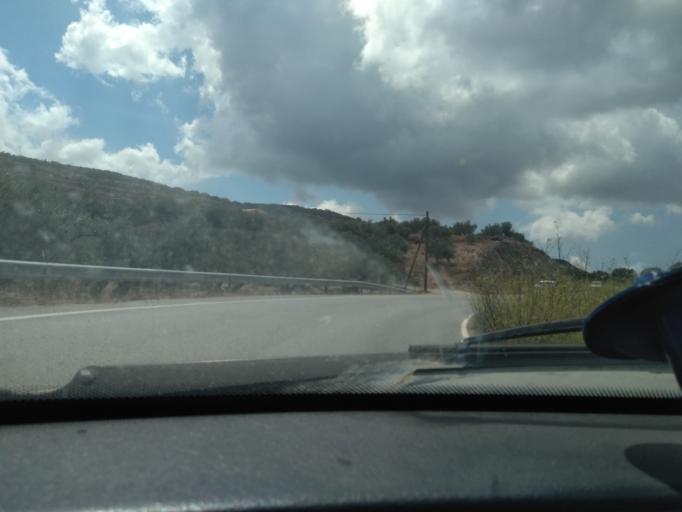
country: GR
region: Crete
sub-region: Nomos Lasithiou
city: Siteia
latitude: 35.1007
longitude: 26.0723
